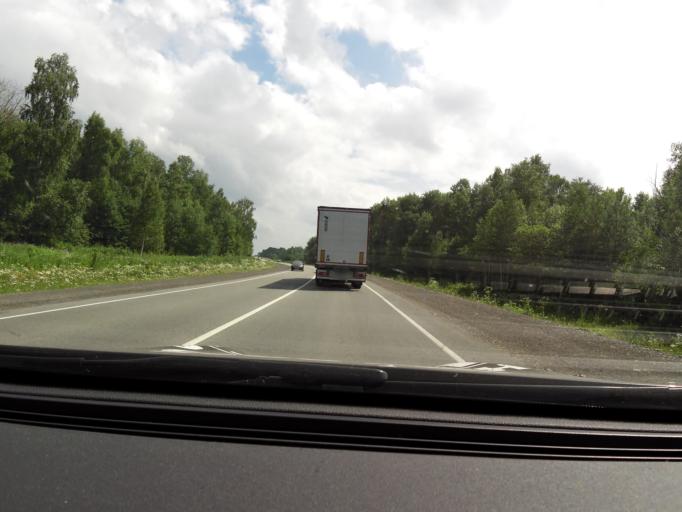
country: RU
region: Perm
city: Suksun
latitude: 56.9968
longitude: 57.4806
